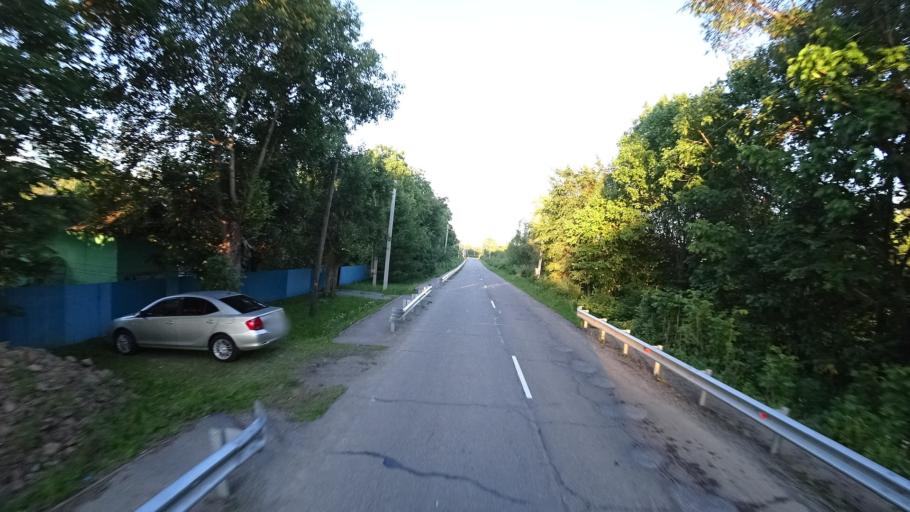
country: RU
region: Khabarovsk Krai
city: Khor
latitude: 47.8540
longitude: 134.9731
